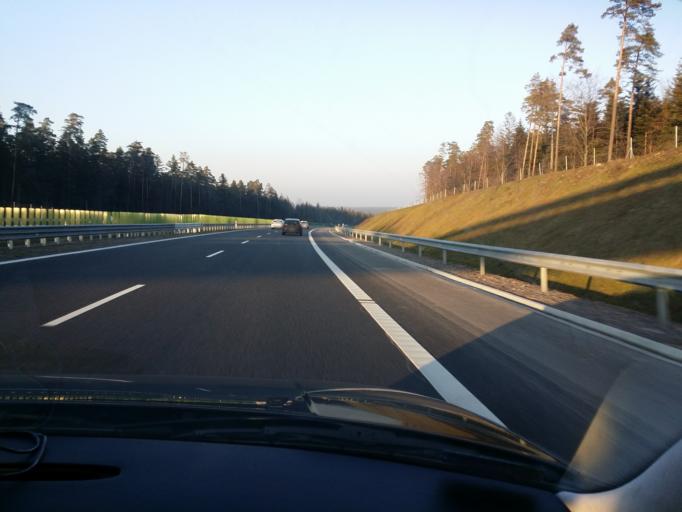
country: PL
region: Swietokrzyskie
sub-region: Powiat skarzyski
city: Skarzysko-Kamienna
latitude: 51.1434
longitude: 20.8337
